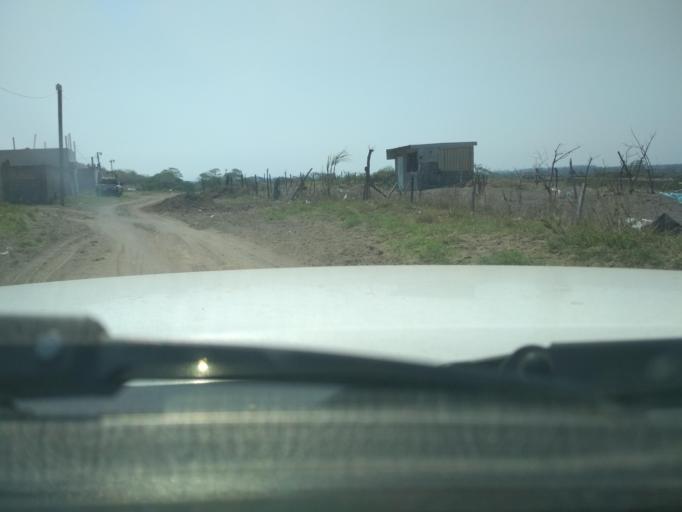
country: MX
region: Veracruz
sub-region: Veracruz
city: Lomas de Rio Medio Cuatro
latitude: 19.1927
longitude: -96.2008
